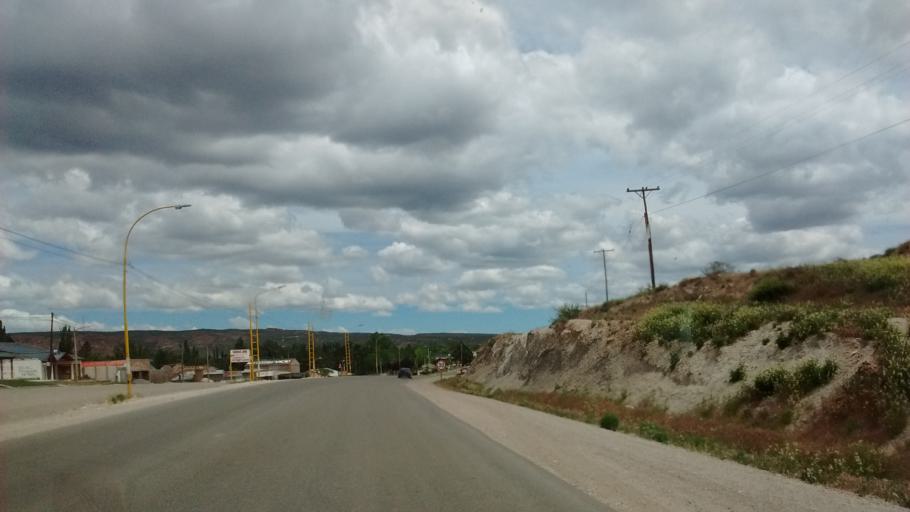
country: AR
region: Neuquen
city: Piedra del Aguila
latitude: -40.0456
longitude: -70.0734
